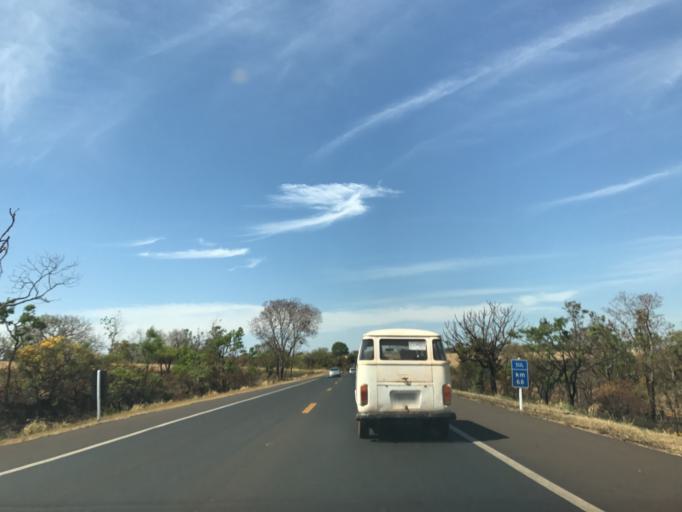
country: BR
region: Minas Gerais
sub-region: Monte Alegre De Minas
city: Monte Alegre de Minas
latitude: -18.9624
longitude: -49.0272
